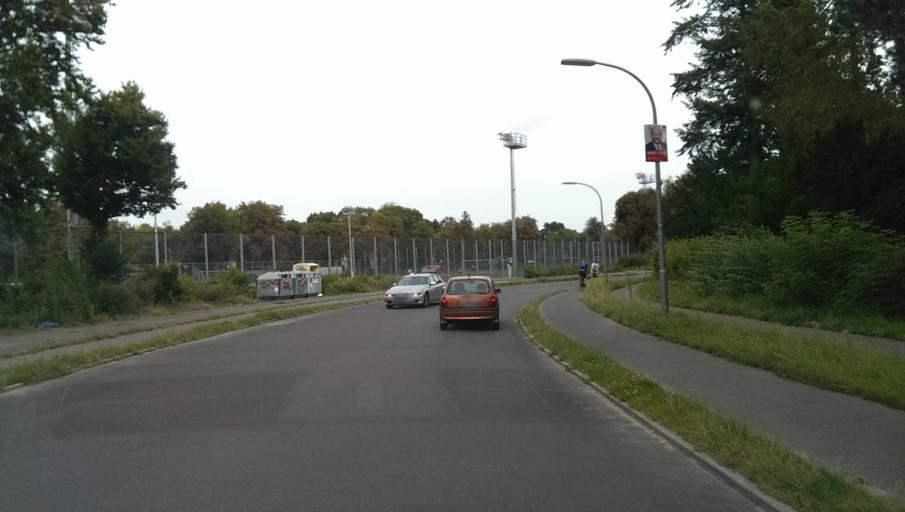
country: DE
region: Berlin
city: Zehlendorf Bezirk
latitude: 52.4413
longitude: 13.2519
